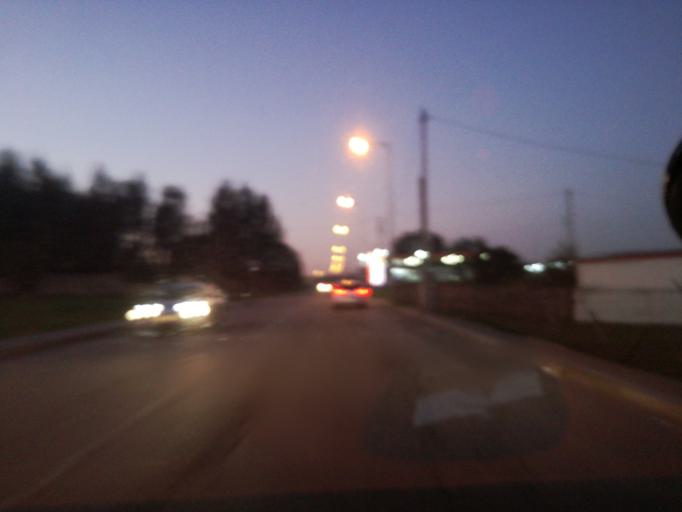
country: PT
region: Porto
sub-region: Valongo
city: Ermesinde
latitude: 41.2226
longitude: -8.5641
